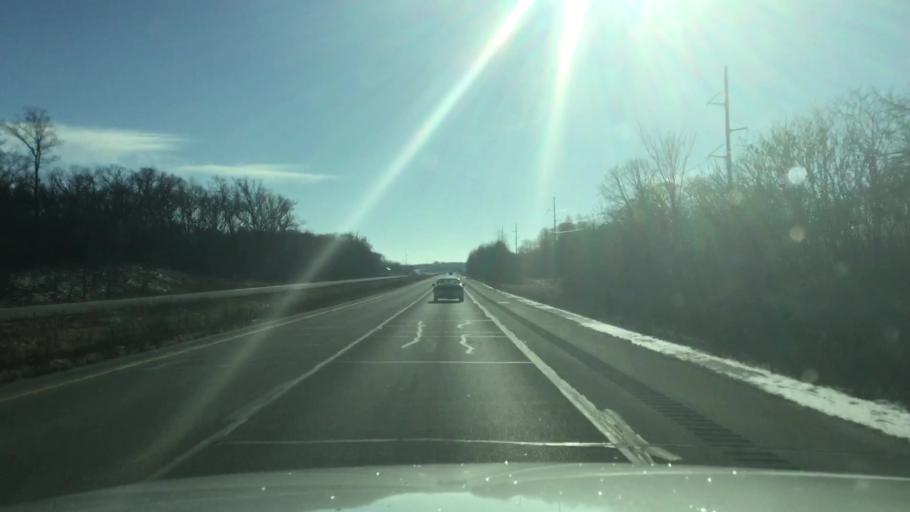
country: US
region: Wisconsin
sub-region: Racine County
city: Rochester
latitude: 42.7328
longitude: -88.2194
